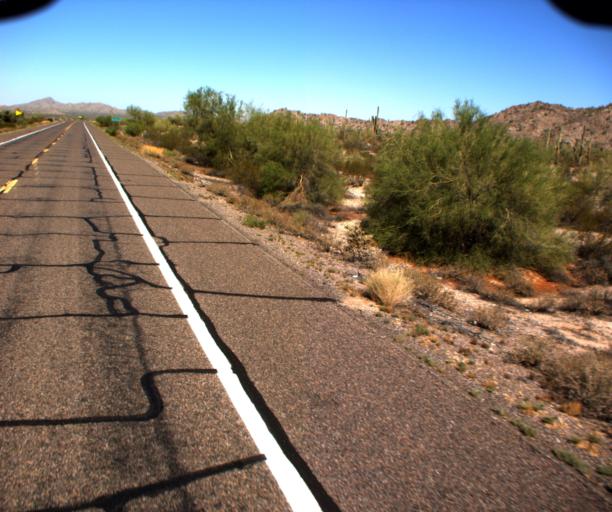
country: US
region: Arizona
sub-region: Pinal County
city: Sacaton
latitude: 33.0034
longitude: -111.7346
